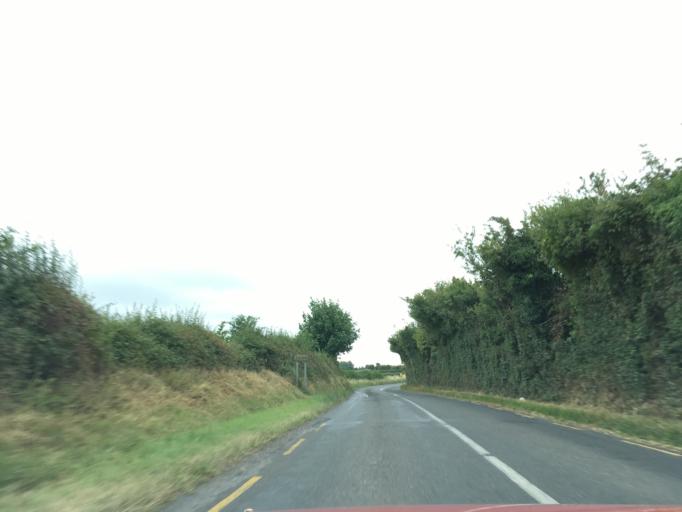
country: IE
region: Munster
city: Cashel
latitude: 52.4562
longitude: -7.8177
